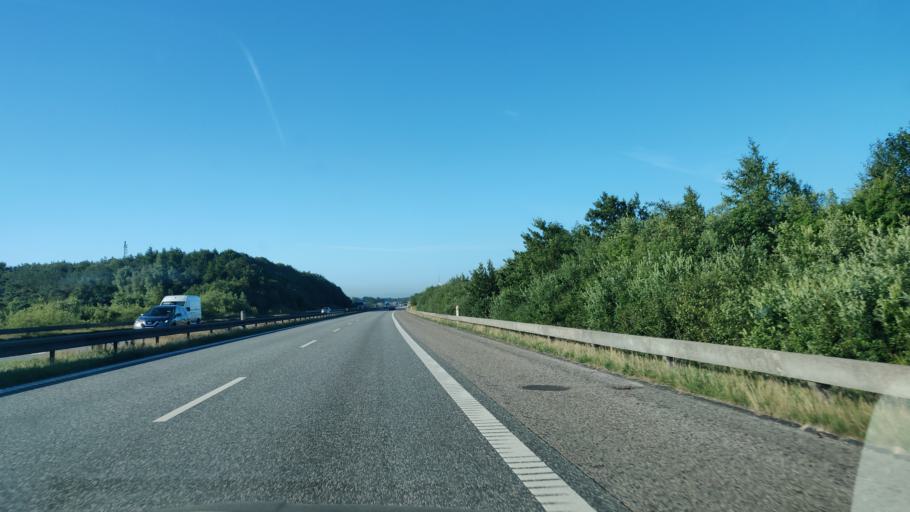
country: DK
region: North Denmark
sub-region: Mariagerfjord Kommune
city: Hobro
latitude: 56.7042
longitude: 9.7294
